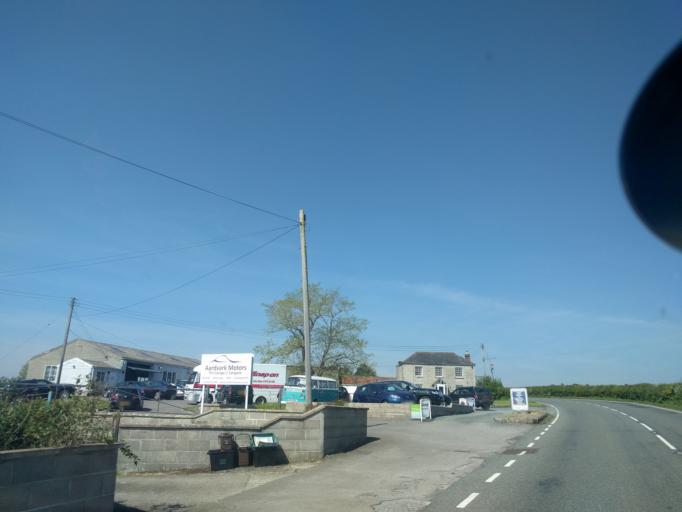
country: GB
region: England
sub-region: Somerset
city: Ilchester
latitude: 51.0297
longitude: -2.7106
